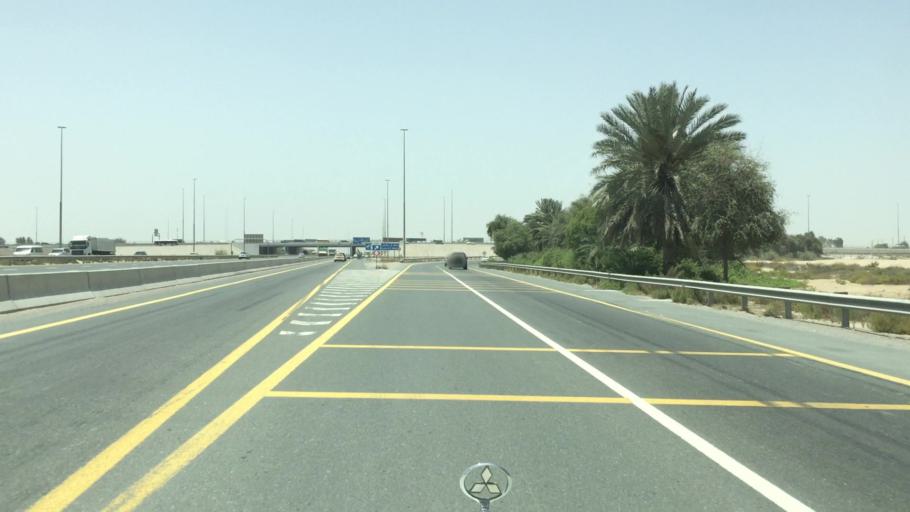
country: AE
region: Dubai
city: Dubai
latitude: 25.1163
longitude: 55.3684
